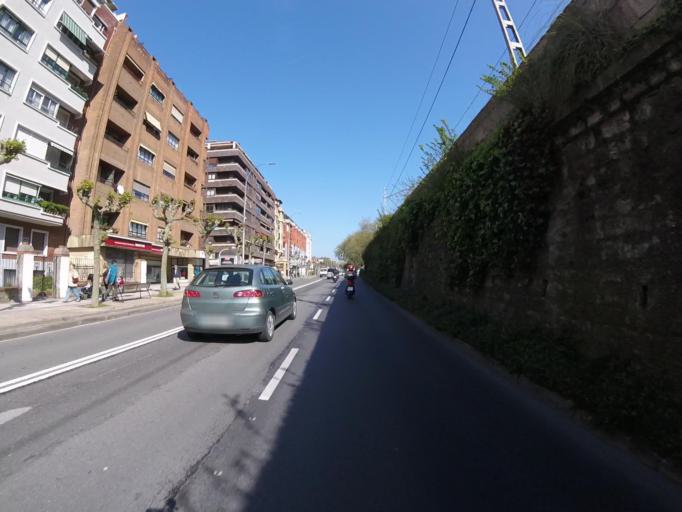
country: ES
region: Basque Country
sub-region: Provincia de Guipuzcoa
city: San Sebastian
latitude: 43.3222
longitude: -1.9688
